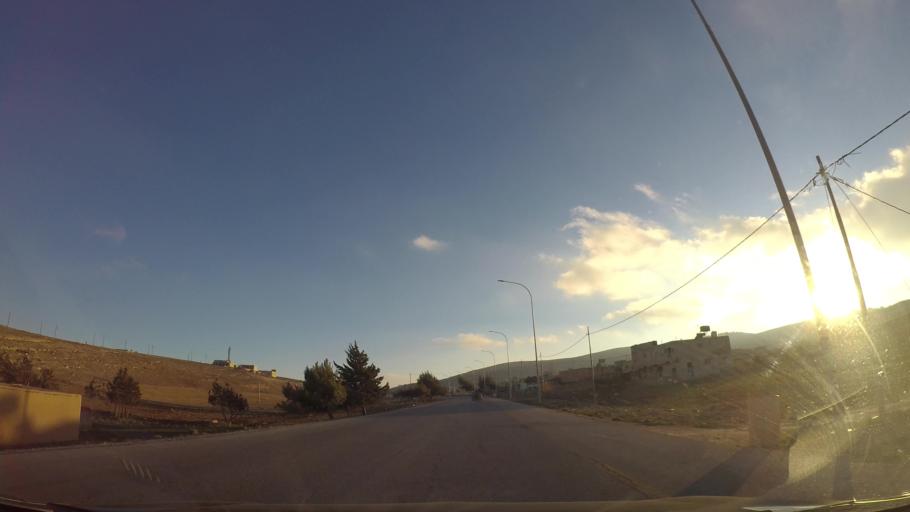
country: JO
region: Ma'an
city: Petra
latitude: 30.4411
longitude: 35.5197
